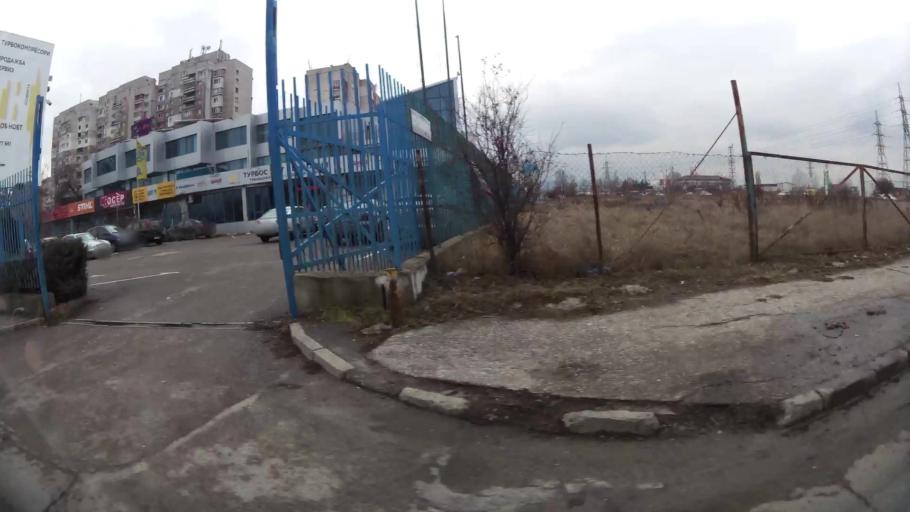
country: BG
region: Sofiya
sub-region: Obshtina Bozhurishte
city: Bozhurishte
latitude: 42.7329
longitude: 23.2512
